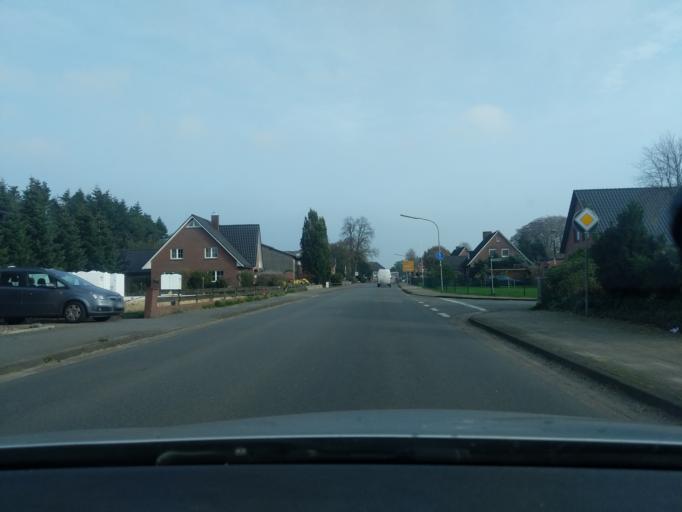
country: DE
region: Lower Saxony
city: Lamstedt
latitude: 53.6367
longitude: 9.0922
